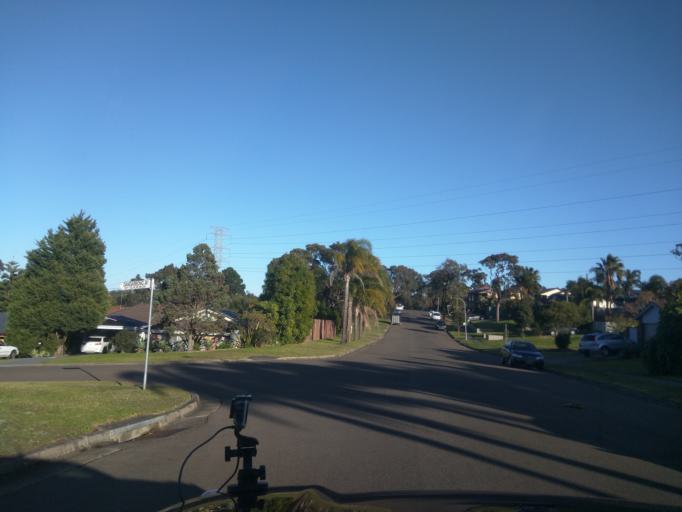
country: AU
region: New South Wales
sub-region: Sutherland Shire
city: Menai
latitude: -34.0203
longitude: 151.0272
